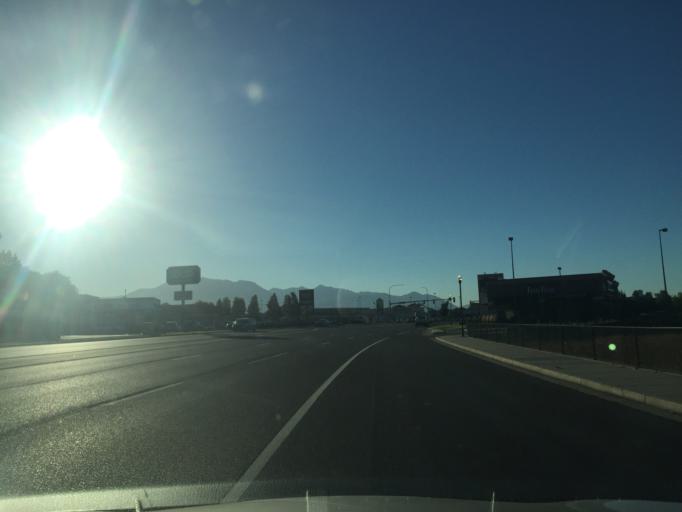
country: US
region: Utah
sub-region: Utah County
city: American Fork
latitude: 40.3844
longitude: -111.8162
